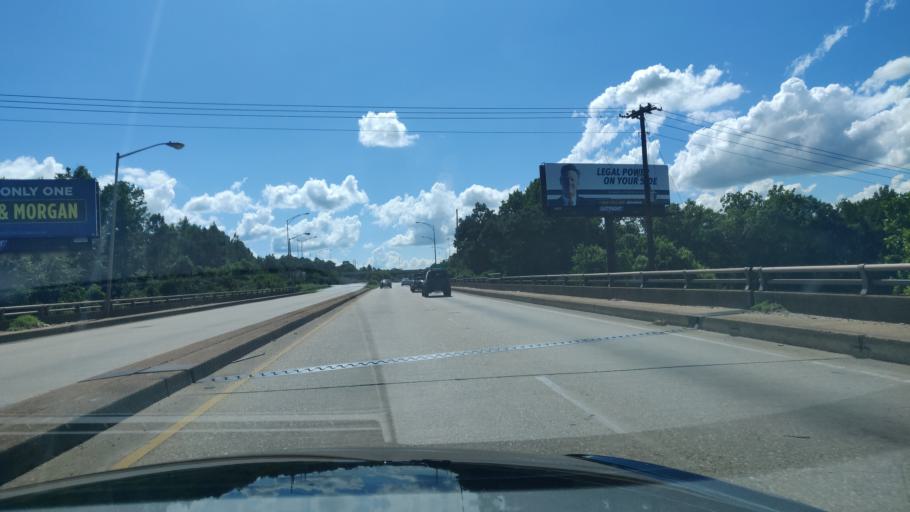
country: US
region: Georgia
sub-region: Muscogee County
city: Columbus
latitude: 32.4531
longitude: -84.9960
